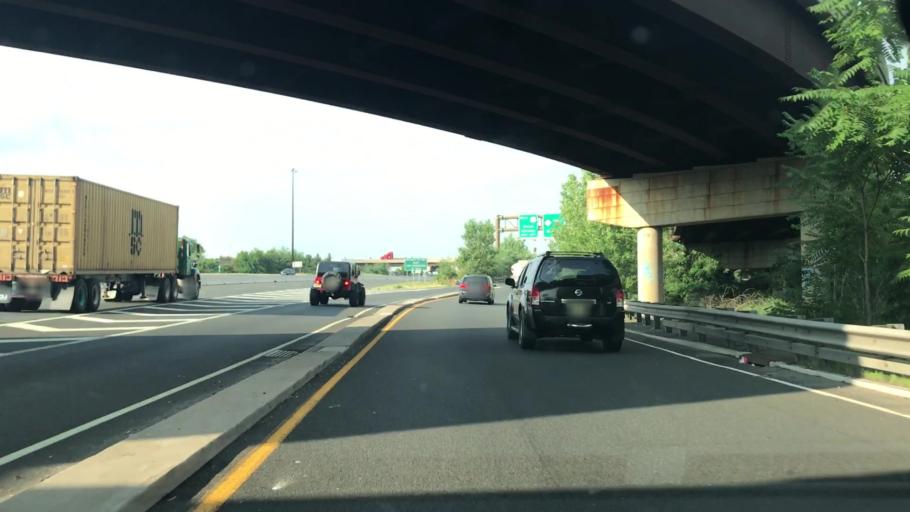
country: US
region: New Jersey
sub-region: Essex County
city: Newark
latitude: 40.7061
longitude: -74.1819
